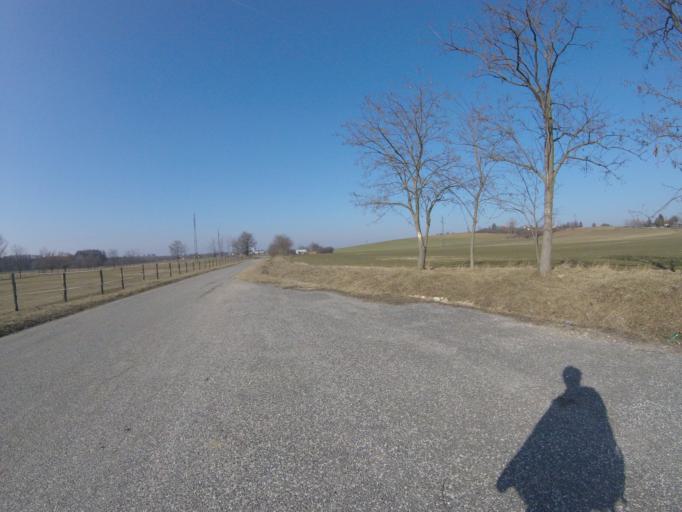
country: HU
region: Komarom-Esztergom
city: Oroszlany
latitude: 47.4721
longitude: 18.3346
